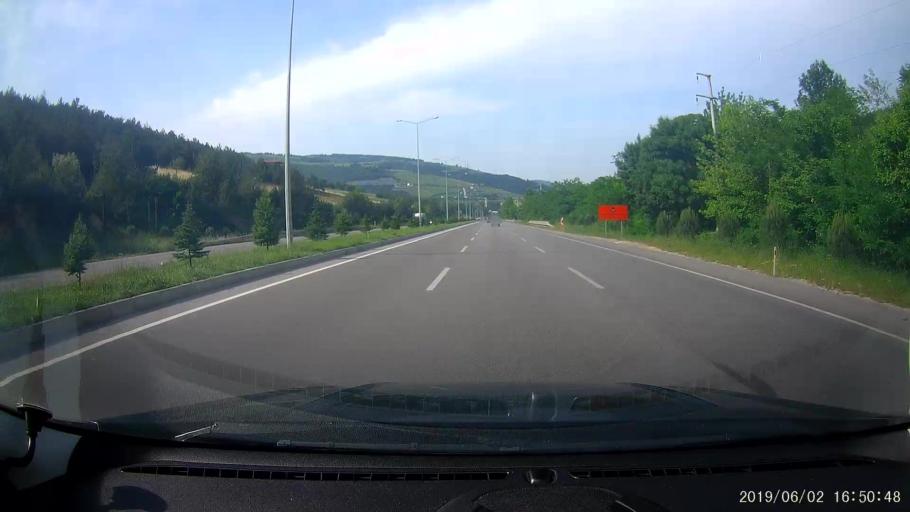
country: TR
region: Samsun
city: Taflan
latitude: 41.2624
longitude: 36.1757
